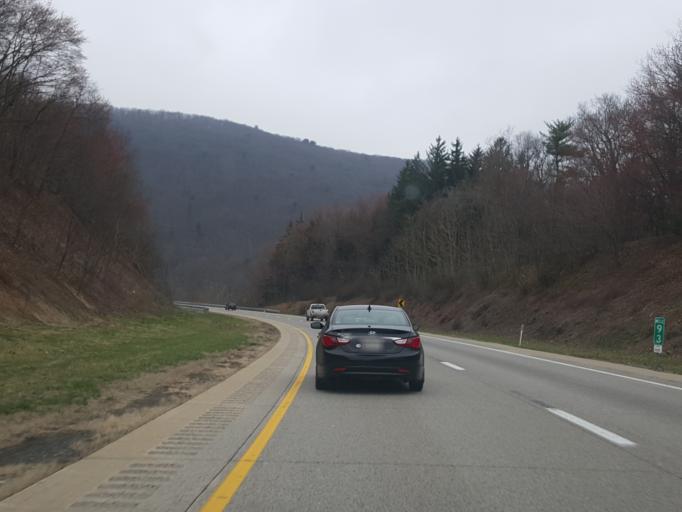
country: US
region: Pennsylvania
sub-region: Lebanon County
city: Jonestown
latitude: 40.4851
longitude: -76.5319
